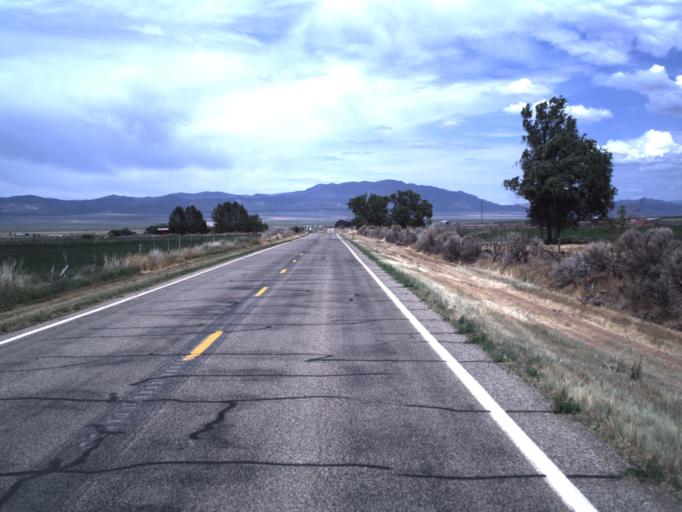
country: US
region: Utah
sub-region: Iron County
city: Parowan
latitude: 37.8938
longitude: -112.7748
